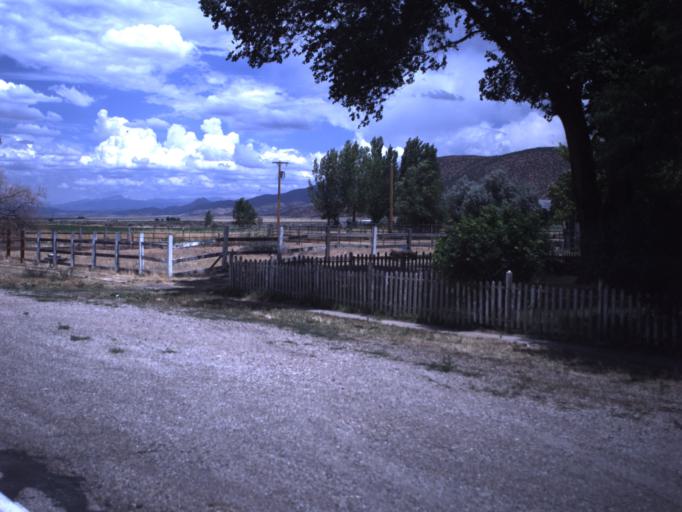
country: US
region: Utah
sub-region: Iron County
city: Parowan
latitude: 37.8902
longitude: -112.7750
